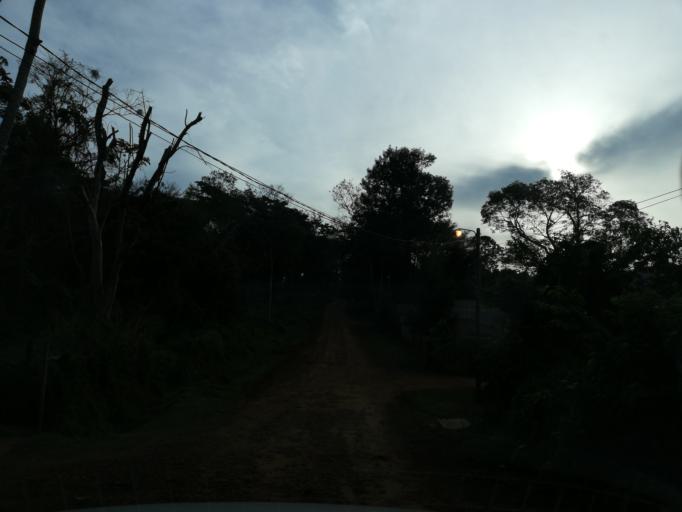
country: AR
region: Misiones
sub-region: Departamento de Capital
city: Posadas
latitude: -27.3558
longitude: -55.9281
